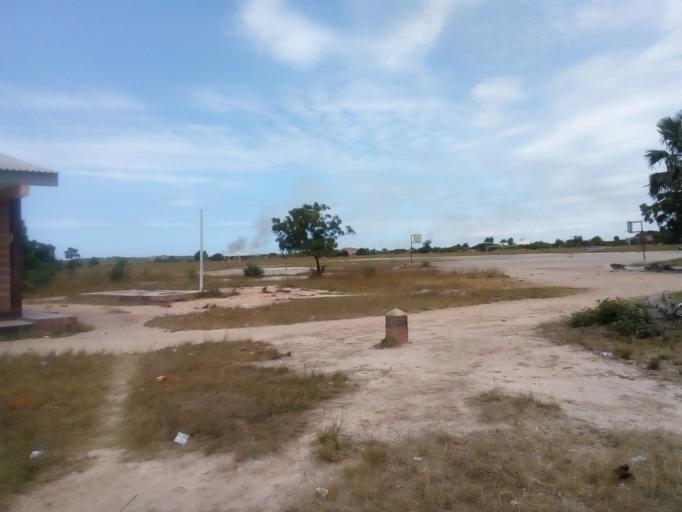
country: GH
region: Volta
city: Anloga
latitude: 5.8004
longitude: 0.6151
